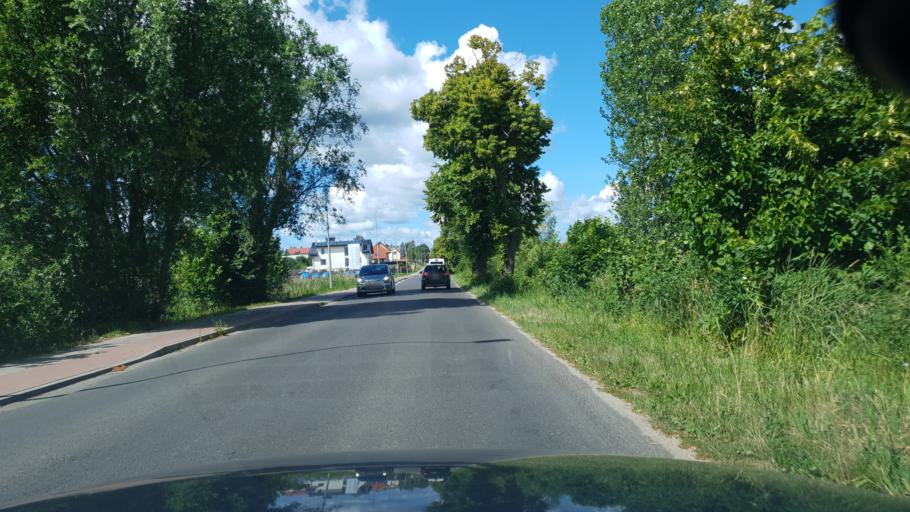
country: PL
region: Pomeranian Voivodeship
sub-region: Powiat pucki
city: Mosty
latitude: 54.6245
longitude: 18.4966
